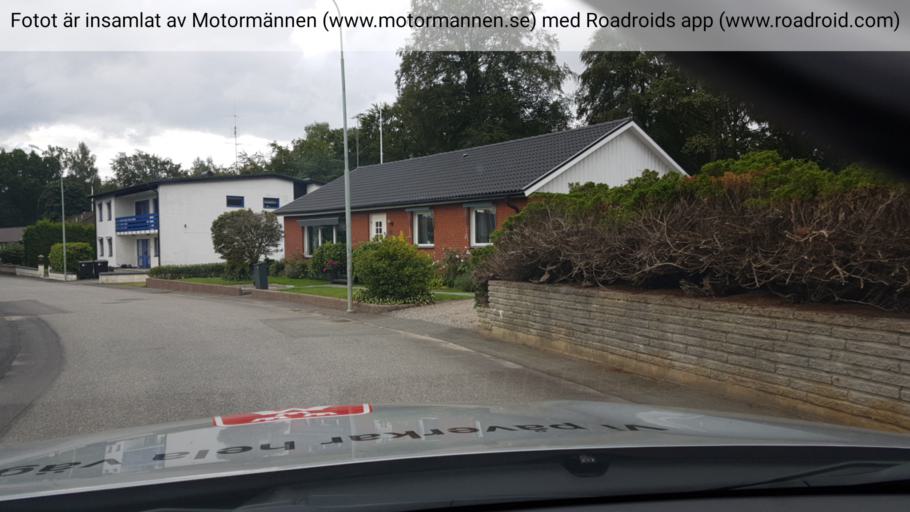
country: SE
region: Skane
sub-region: Hassleholms Kommun
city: Hassleholm
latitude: 56.1557
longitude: 13.7441
